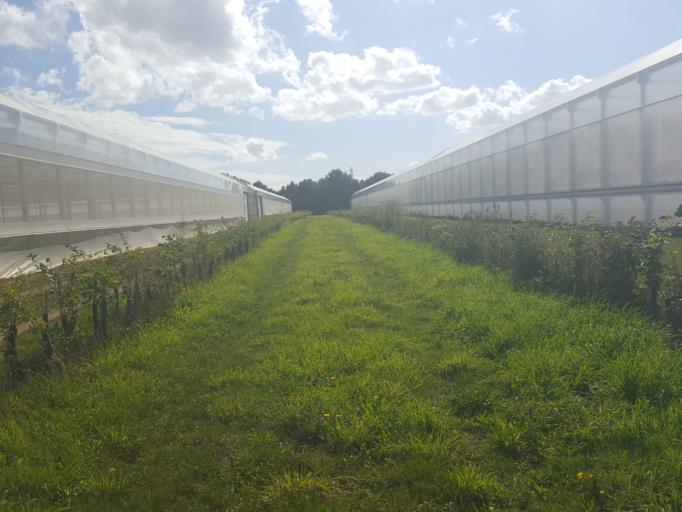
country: GB
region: England
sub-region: Essex
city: Alresford
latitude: 51.8544
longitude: 1.0198
